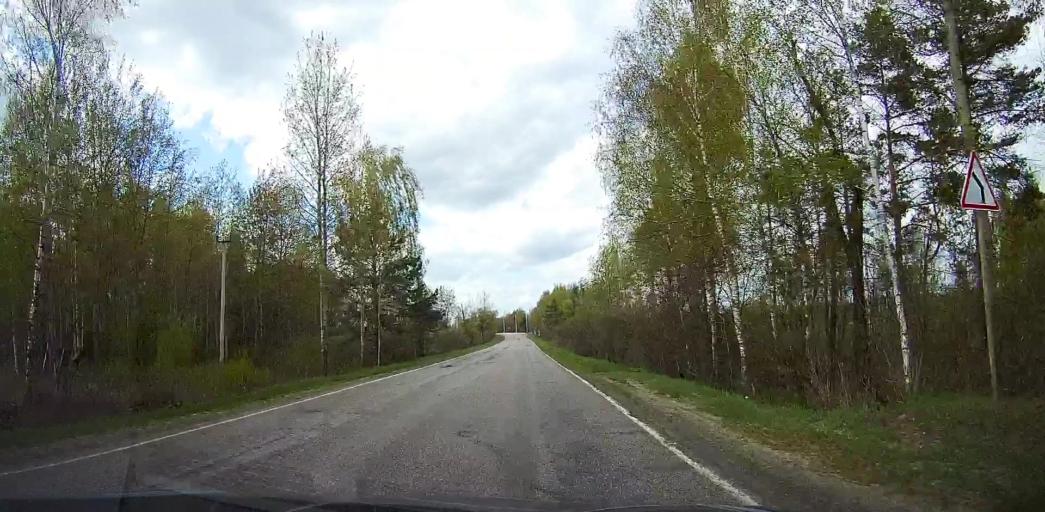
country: RU
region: Moskovskaya
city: Davydovo
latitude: 55.6619
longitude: 38.8077
